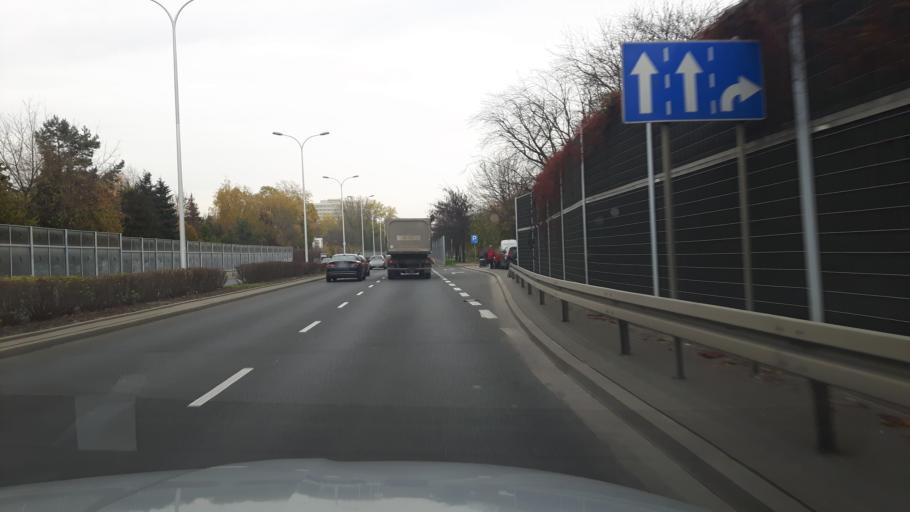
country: PL
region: Masovian Voivodeship
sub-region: Warszawa
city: Ursynow
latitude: 52.1721
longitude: 21.0579
